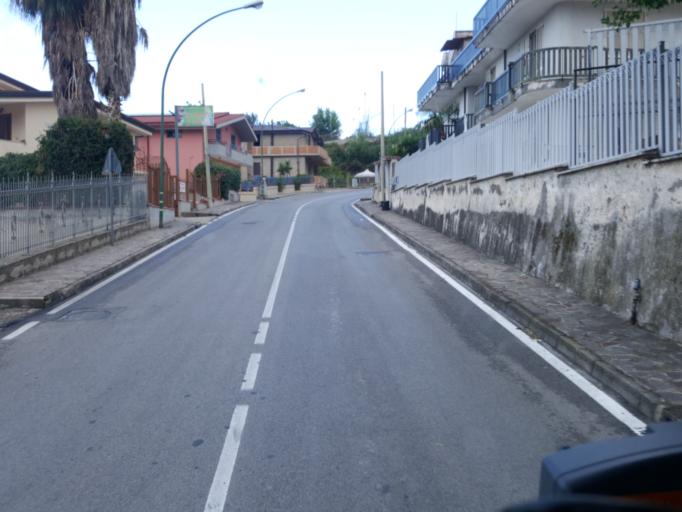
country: IT
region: Campania
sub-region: Provincia di Avellino
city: Domicella
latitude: 40.8792
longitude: 14.5845
